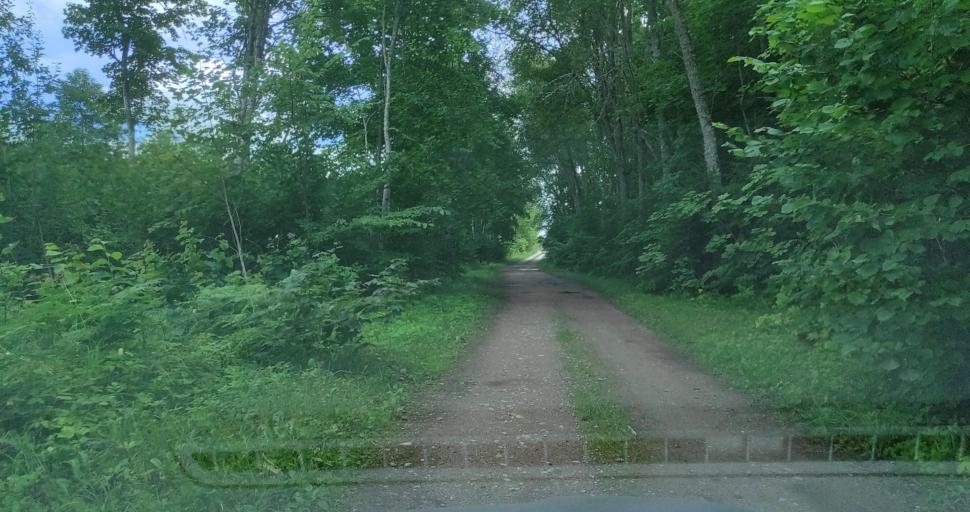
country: LV
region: Kuldigas Rajons
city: Kuldiga
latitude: 56.9897
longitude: 21.7711
